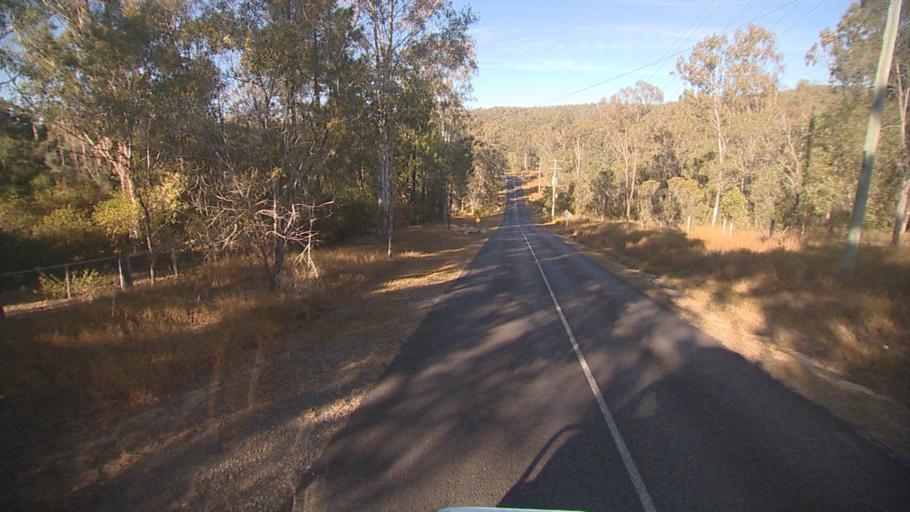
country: AU
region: Queensland
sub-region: Logan
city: Cedar Vale
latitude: -27.8414
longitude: 153.0831
